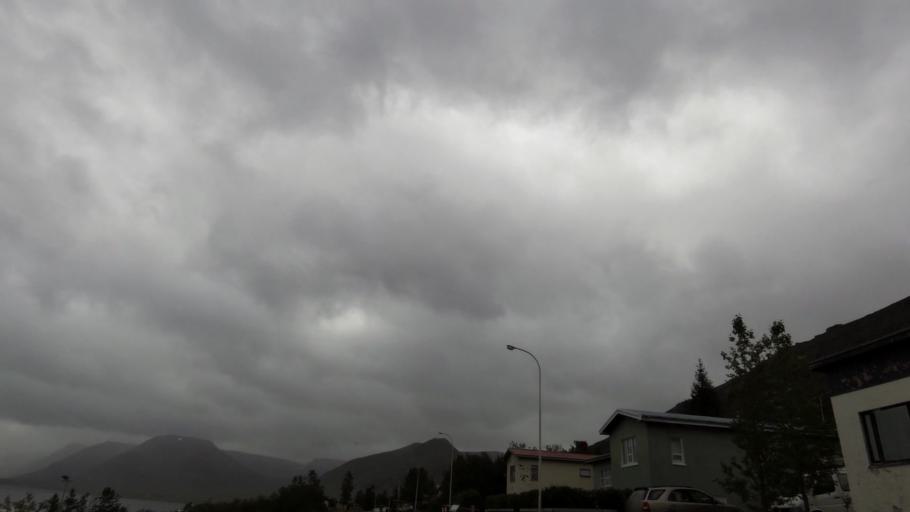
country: IS
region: Westfjords
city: Isafjoerdur
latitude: 65.8749
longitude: -23.4888
